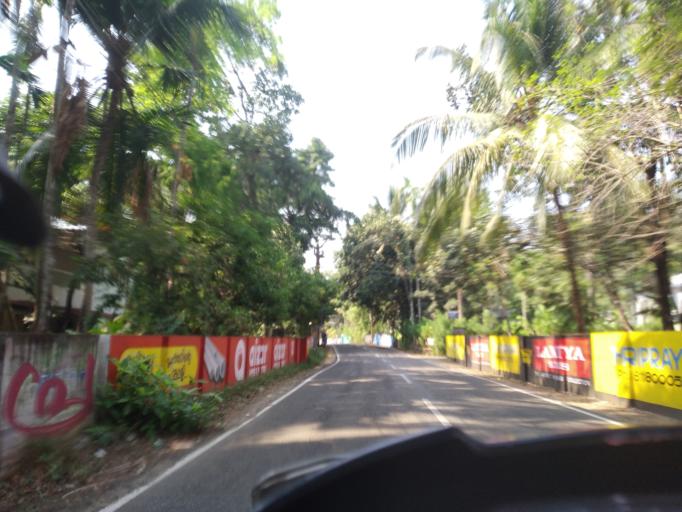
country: IN
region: Kerala
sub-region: Thrissur District
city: Thanniyam
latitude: 10.4333
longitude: 76.0819
